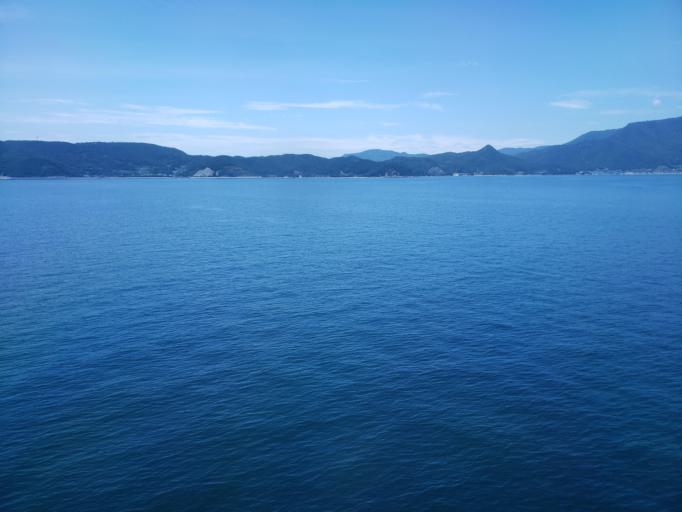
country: JP
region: Kagawa
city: Tonosho
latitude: 34.4273
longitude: 134.2778
